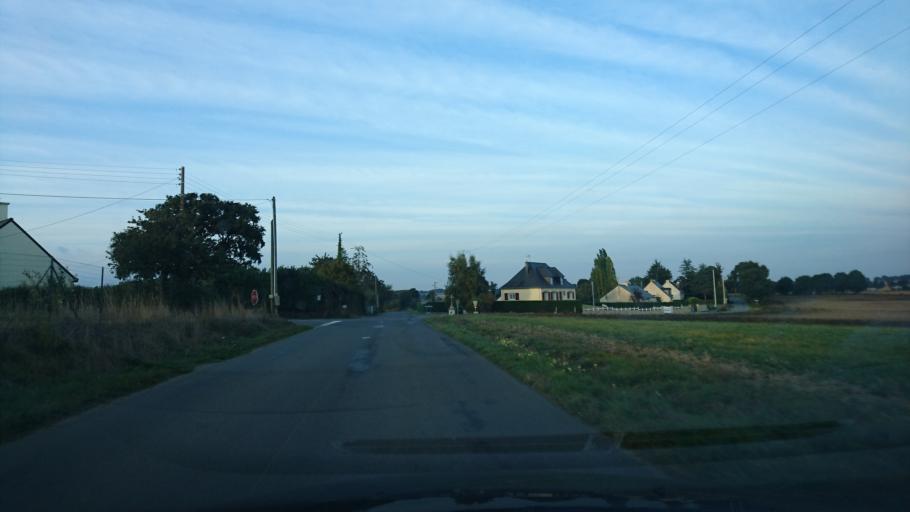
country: FR
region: Brittany
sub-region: Departement d'Ille-et-Vilaine
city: Sixt-sur-Aff
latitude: 47.7893
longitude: -2.0649
